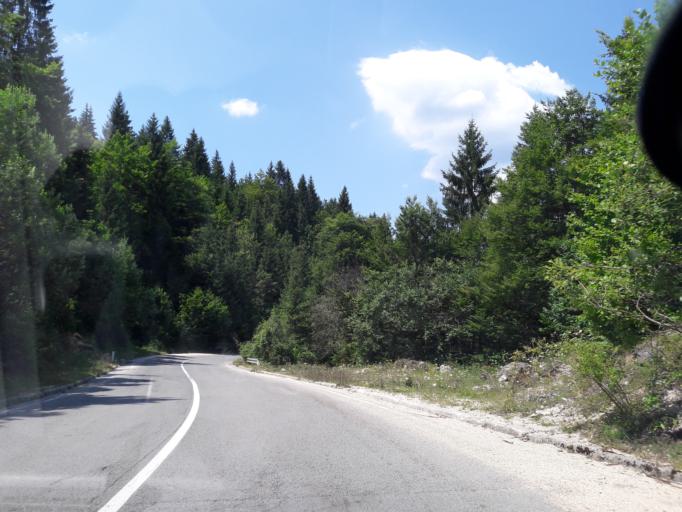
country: BA
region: Republika Srpska
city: Sipovo
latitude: 44.1289
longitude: 17.1810
